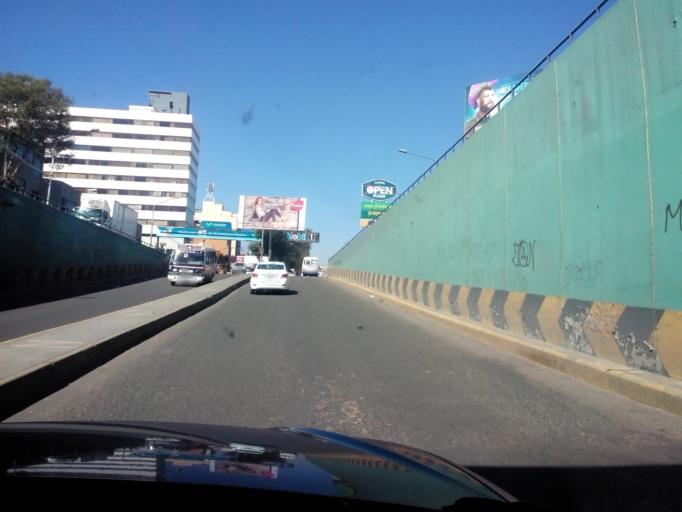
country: PE
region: Arequipa
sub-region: Provincia de Arequipa
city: Arequipa
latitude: -16.3898
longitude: -71.5473
